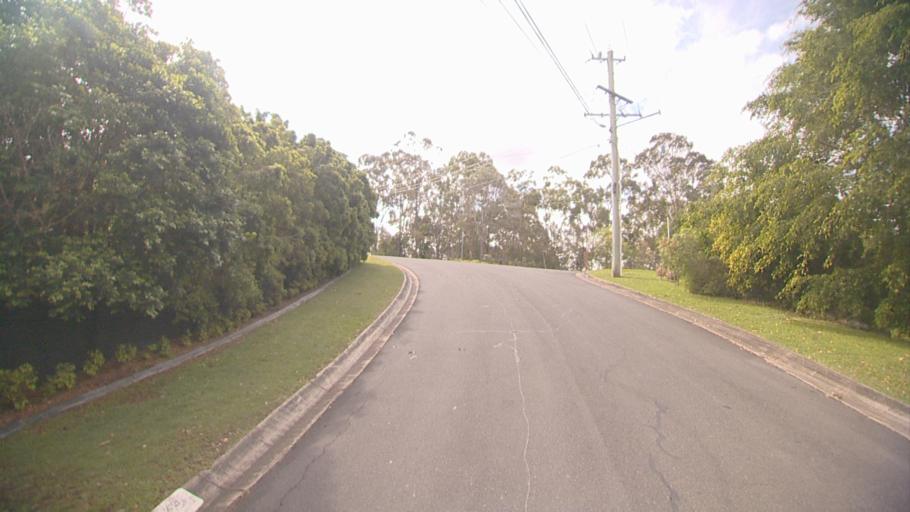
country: AU
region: Queensland
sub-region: Logan
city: Slacks Creek
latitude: -27.6621
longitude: 153.1961
